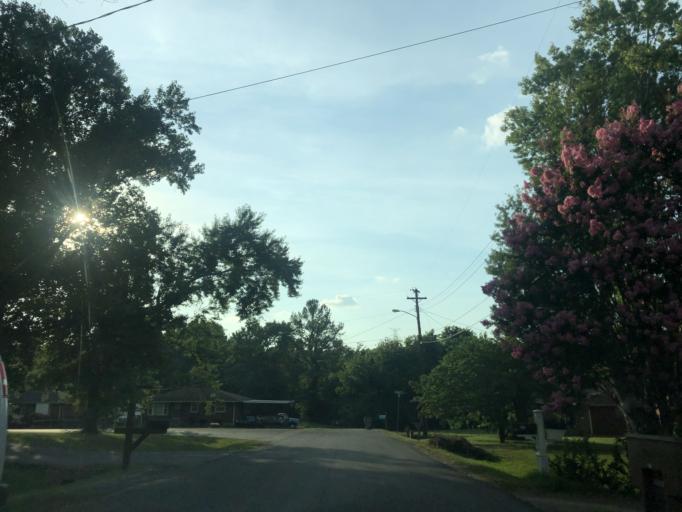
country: US
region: Tennessee
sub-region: Davidson County
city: Nashville
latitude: 36.1568
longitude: -86.6965
